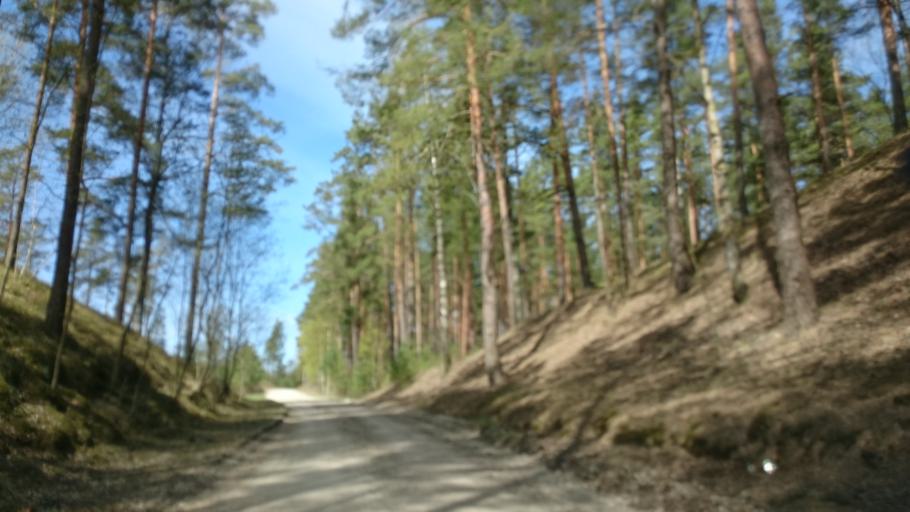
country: LV
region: Carnikava
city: Carnikava
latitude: 57.1696
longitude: 24.3606
